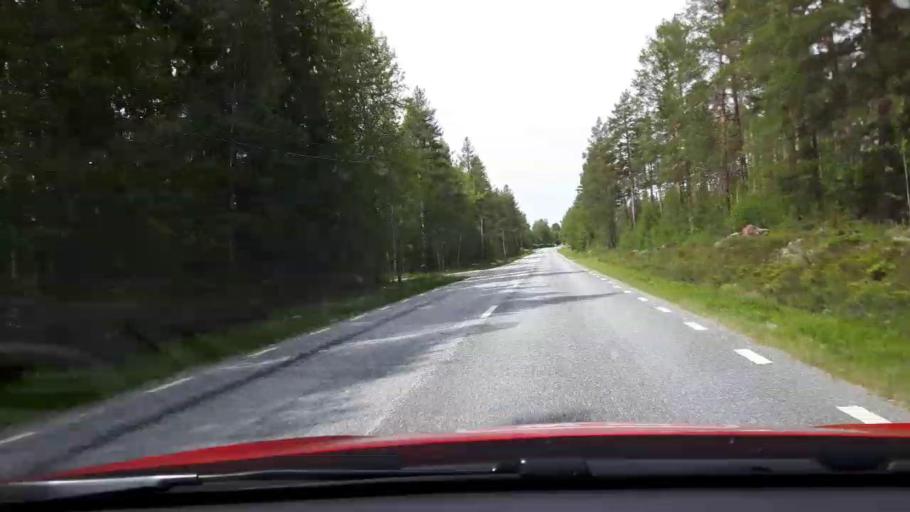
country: SE
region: Jaemtland
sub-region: Harjedalens Kommun
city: Sveg
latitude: 62.1519
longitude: 13.9002
